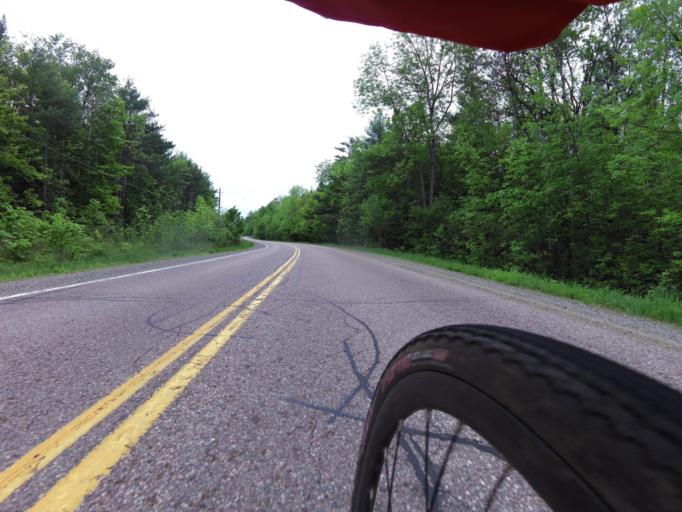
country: CA
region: Ontario
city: Renfrew
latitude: 45.2930
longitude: -76.7001
